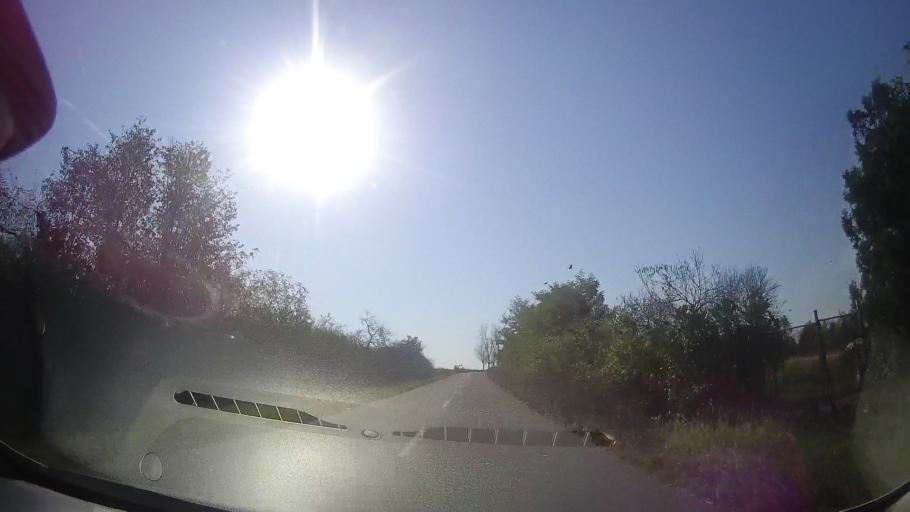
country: RO
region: Timis
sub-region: Comuna Topolovatu Mare
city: Topolovatu Mare
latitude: 45.8121
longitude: 21.5829
